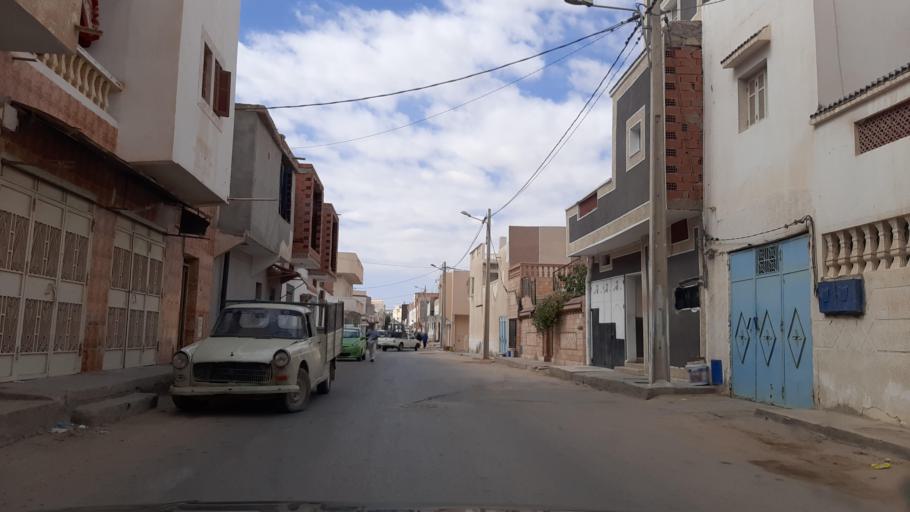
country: TN
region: Tataouine
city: Tataouine
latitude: 32.9294
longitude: 10.4565
